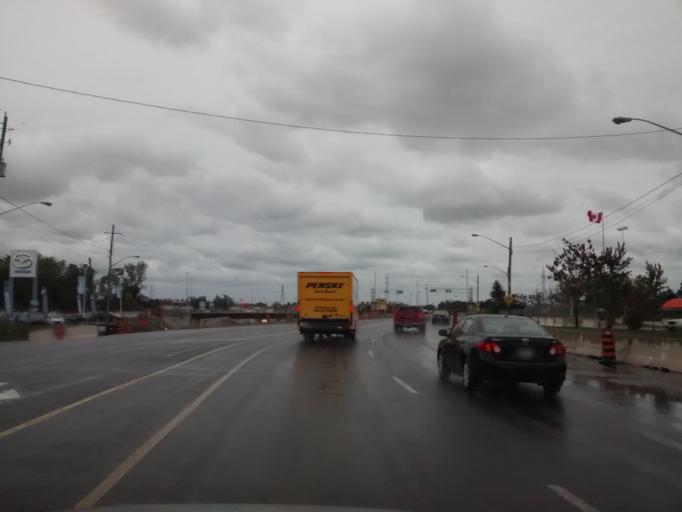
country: CA
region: Ontario
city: Hamilton
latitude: 43.2400
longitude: -79.7591
